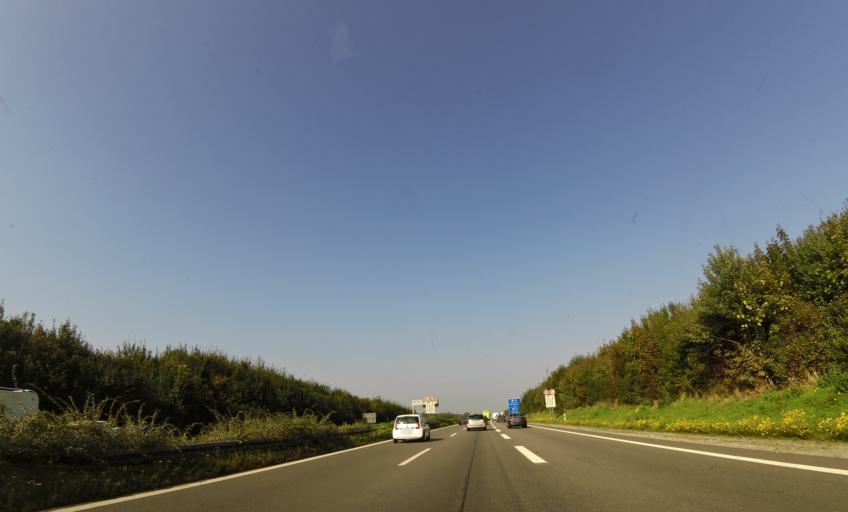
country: DE
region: Baden-Wuerttemberg
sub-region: Regierungsbezirk Stuttgart
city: Erlenbach
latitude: 49.1718
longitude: 9.2485
